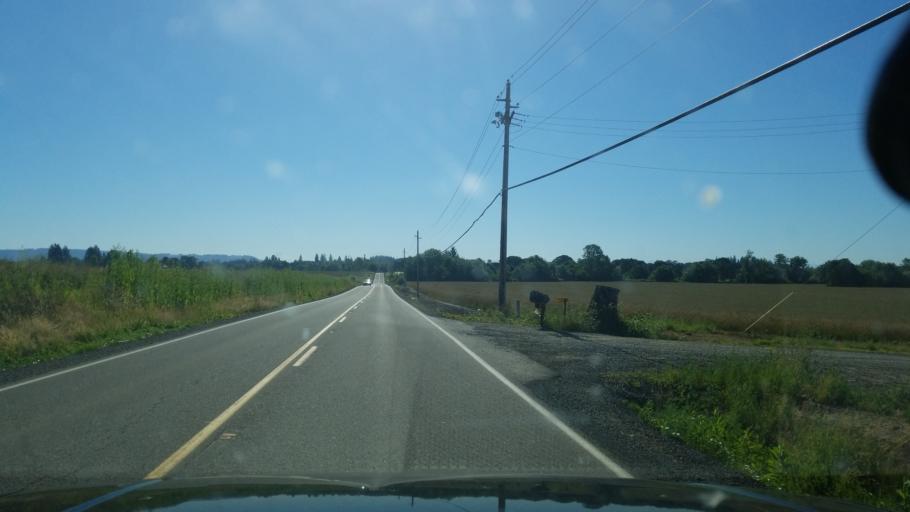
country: US
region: Oregon
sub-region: Yamhill County
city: McMinnville
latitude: 45.2305
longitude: -123.2433
